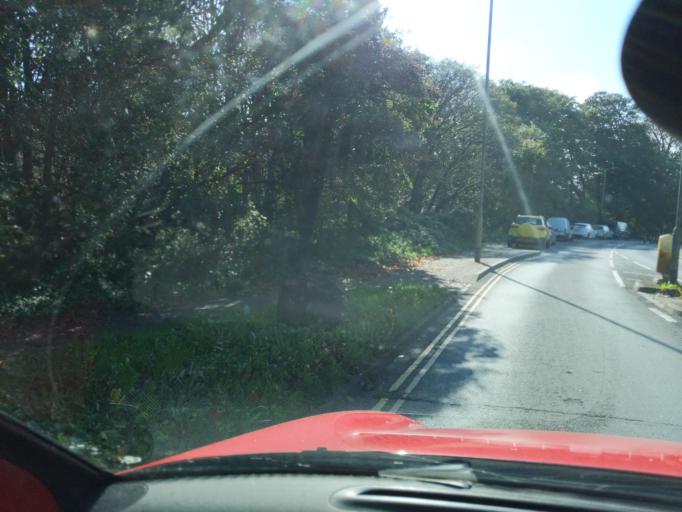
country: GB
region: England
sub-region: Plymouth
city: Plymouth
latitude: 50.4254
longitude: -4.1356
